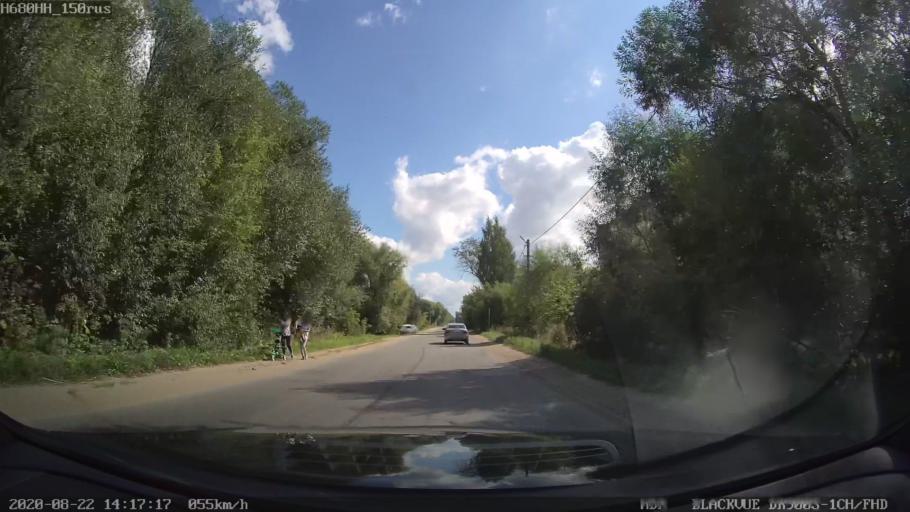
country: RU
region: Tverskaya
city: Bezhetsk
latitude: 57.7702
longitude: 36.7042
